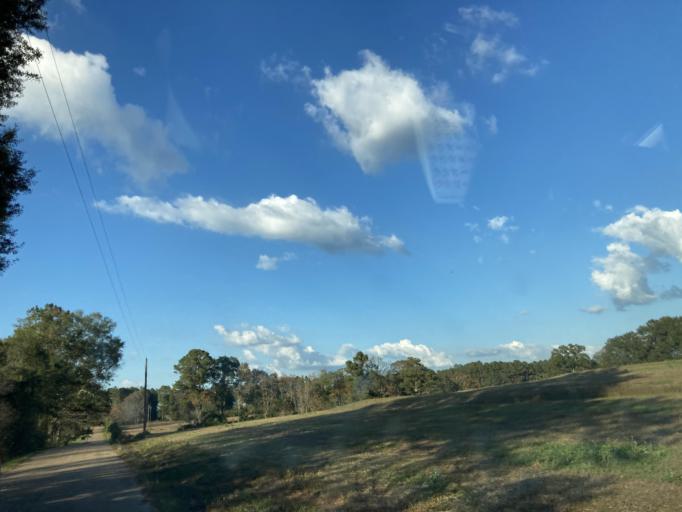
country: US
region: Mississippi
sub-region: Lamar County
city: Sumrall
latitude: 31.3993
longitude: -89.6200
